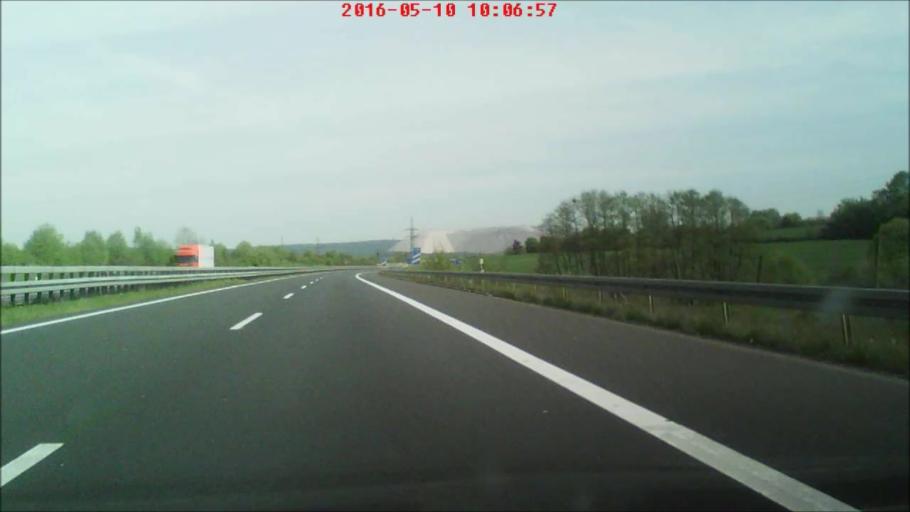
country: DE
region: Hesse
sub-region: Regierungsbezirk Kassel
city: Flieden
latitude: 50.4117
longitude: 9.5711
